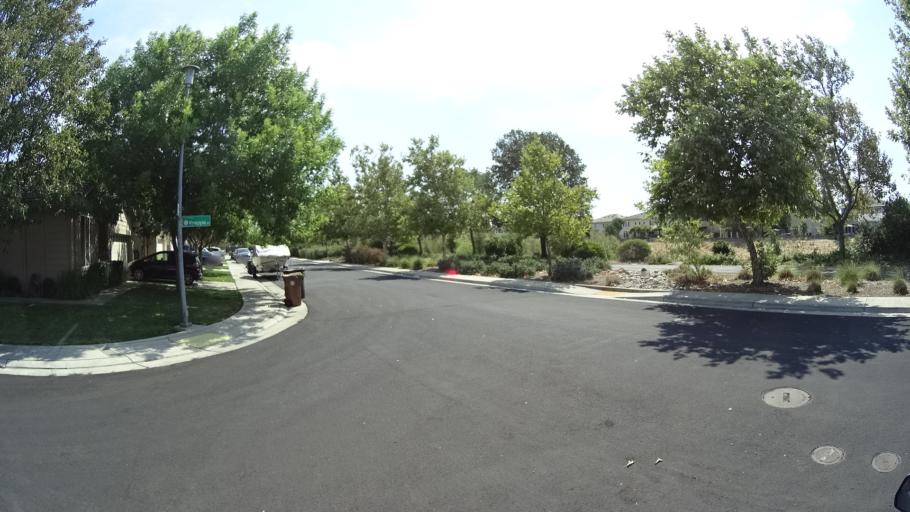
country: US
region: California
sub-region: Sacramento County
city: Laguna
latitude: 38.3846
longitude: -121.4472
